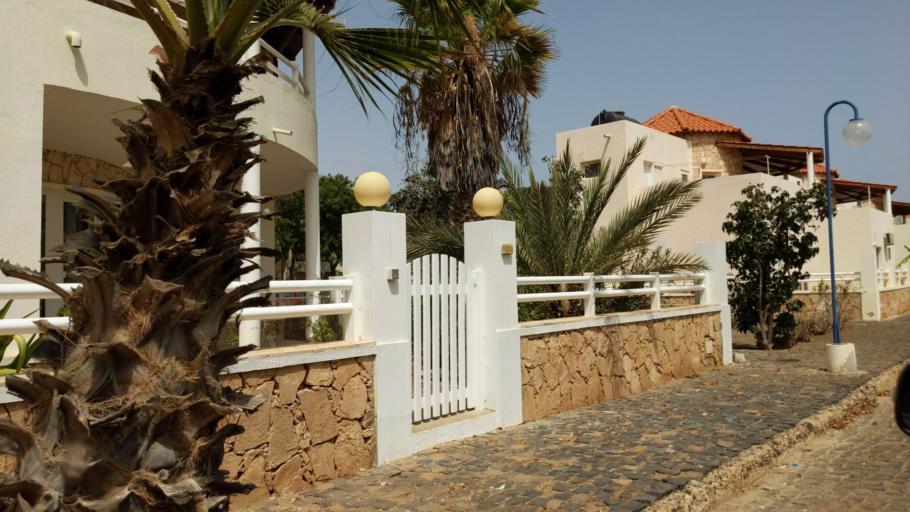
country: CV
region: Sal
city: Espargos
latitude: 16.6811
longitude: -22.9368
